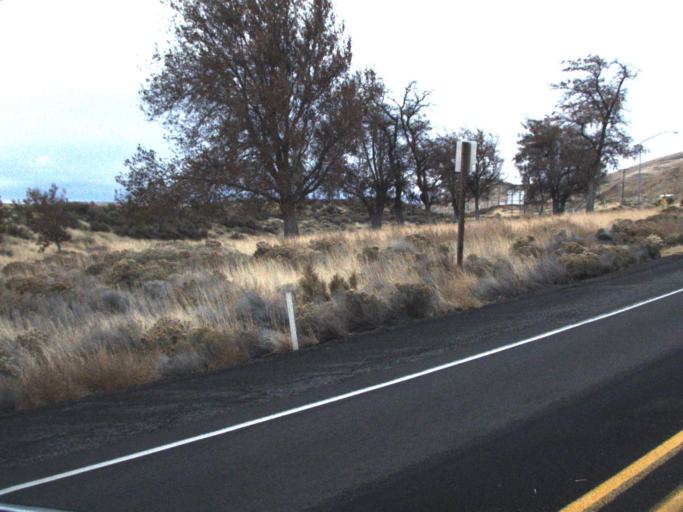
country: US
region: Washington
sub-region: Benton County
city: Finley
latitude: 46.0568
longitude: -118.9088
